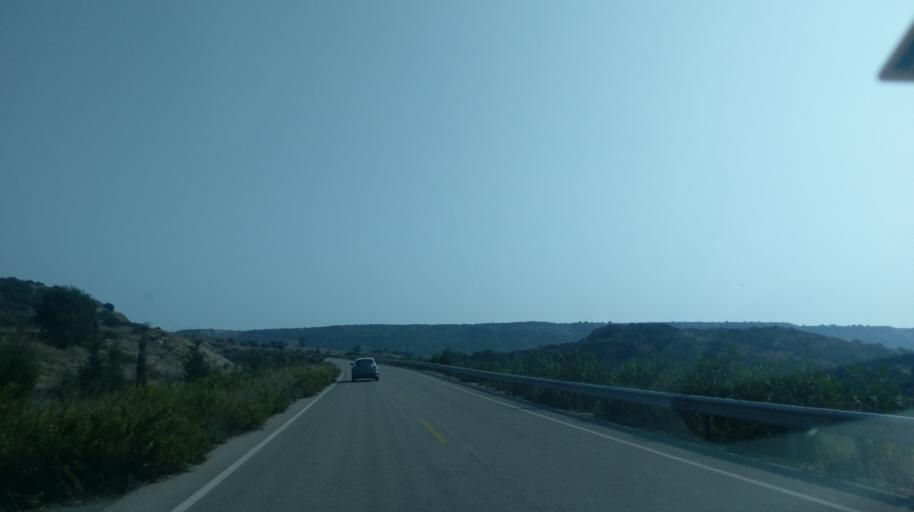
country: CY
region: Ammochostos
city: Leonarisso
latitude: 35.4783
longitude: 34.1152
